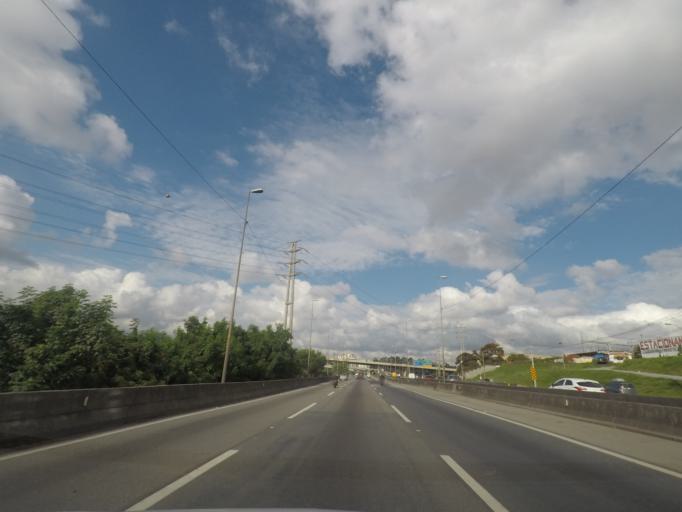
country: BR
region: Sao Paulo
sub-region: Osasco
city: Osasco
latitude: -23.5259
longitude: -46.7540
